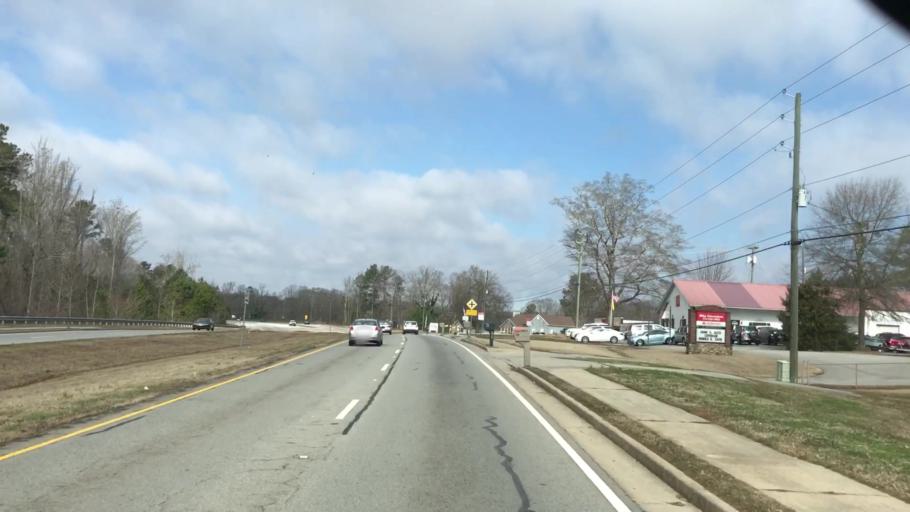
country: US
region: Georgia
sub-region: Hall County
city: Oakwood
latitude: 34.2046
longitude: -83.8562
